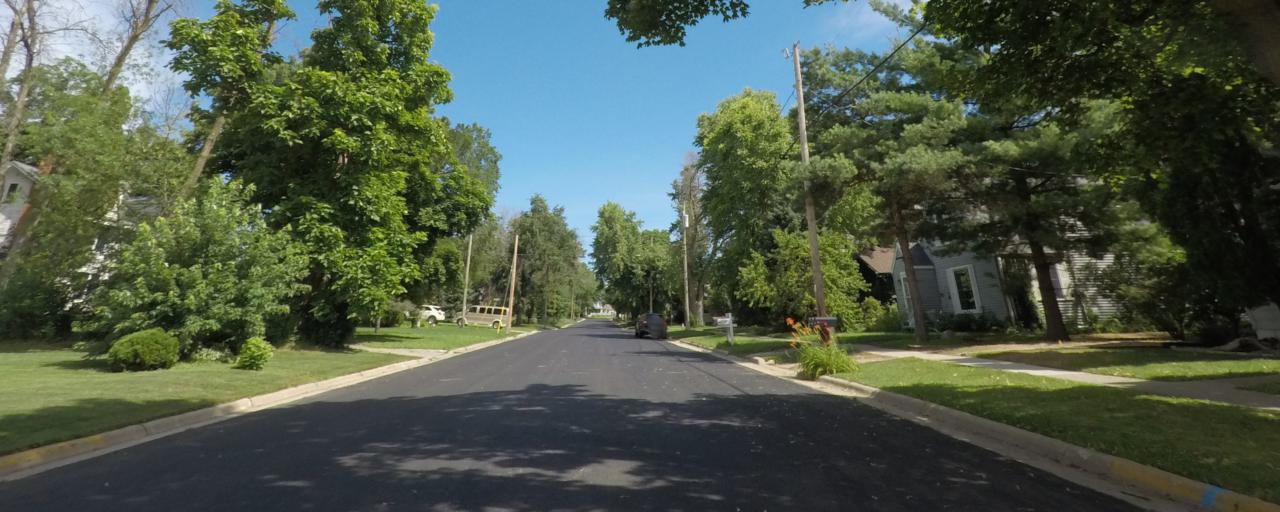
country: US
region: Wisconsin
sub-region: Dane County
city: McFarland
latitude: 43.0157
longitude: -89.2887
